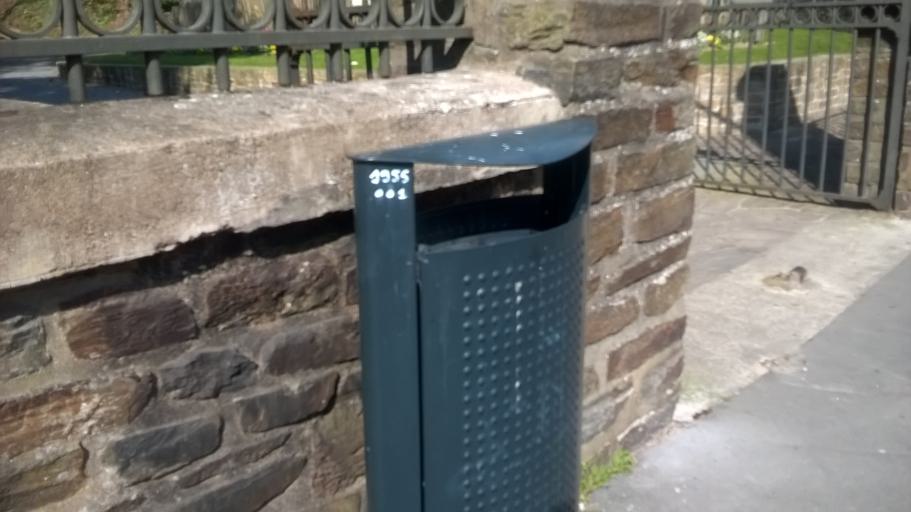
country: FR
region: Pays de la Loire
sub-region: Departement de la Loire-Atlantique
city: Nantes
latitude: 47.2338
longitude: -1.5359
